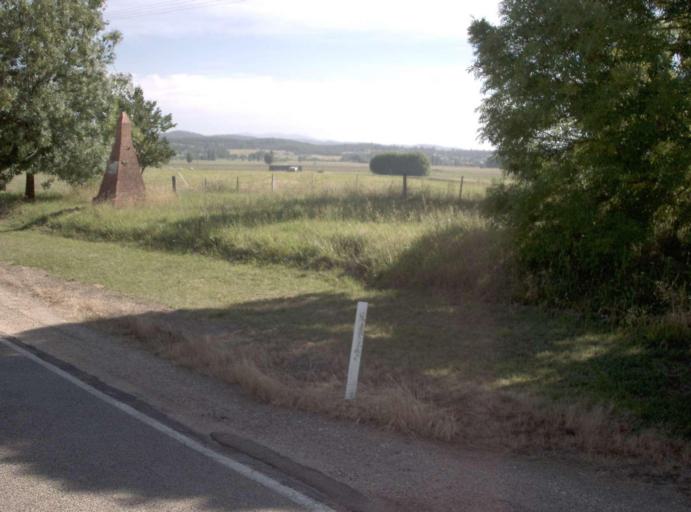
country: AU
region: Victoria
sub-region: East Gippsland
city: Bairnsdale
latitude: -37.7326
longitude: 147.8111
